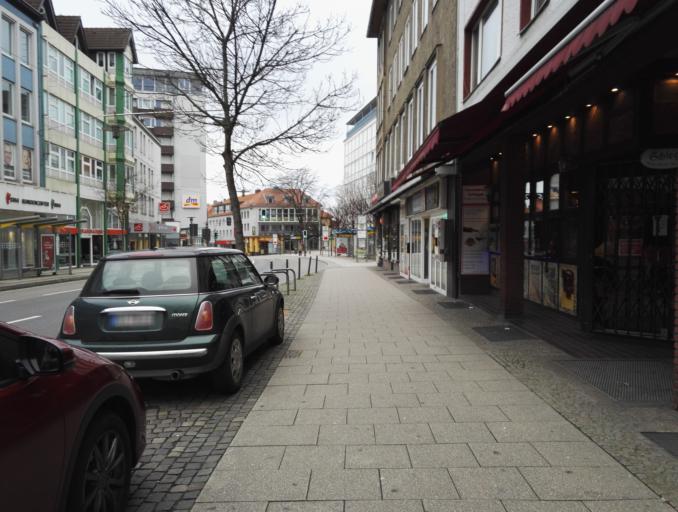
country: DE
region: Lower Saxony
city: Hildesheim
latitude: 52.1507
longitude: 9.9523
